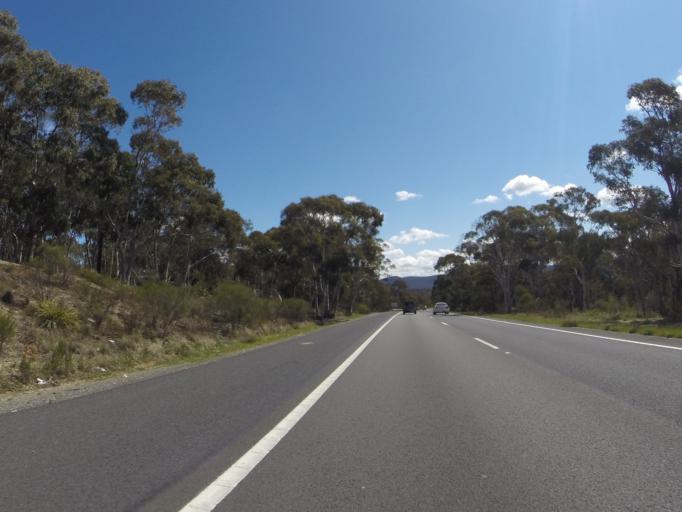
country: AU
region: New South Wales
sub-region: Goulburn Mulwaree
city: Goulburn
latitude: -34.7423
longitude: 149.8400
